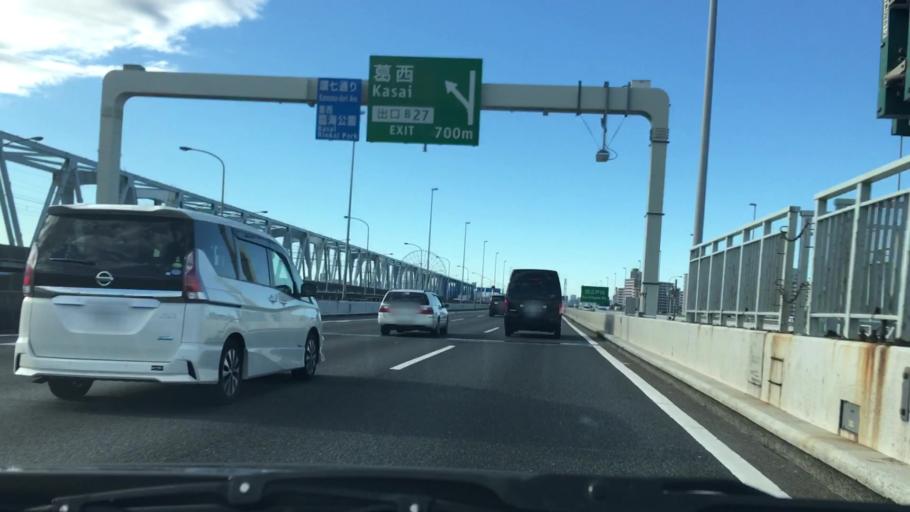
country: JP
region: Tokyo
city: Urayasu
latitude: 35.6391
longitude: 139.8778
